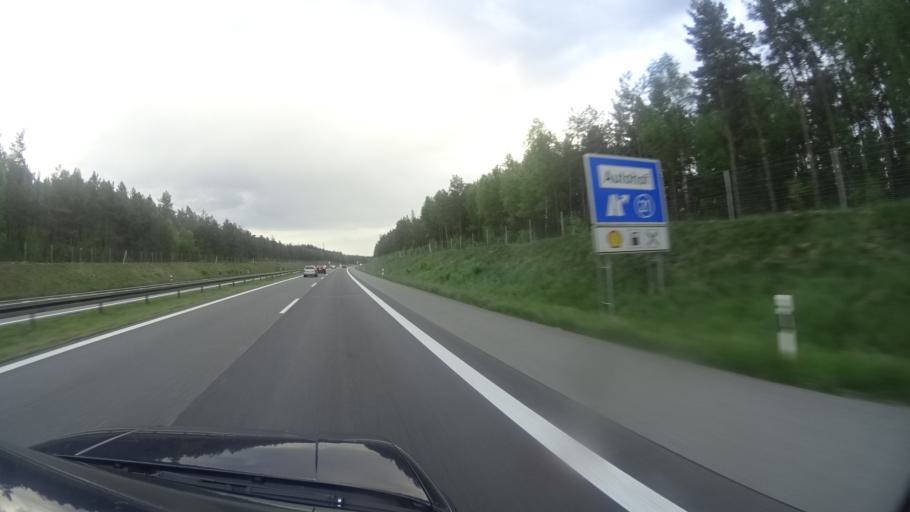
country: DE
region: Brandenburg
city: Wittstock
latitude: 53.0916
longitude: 12.5102
